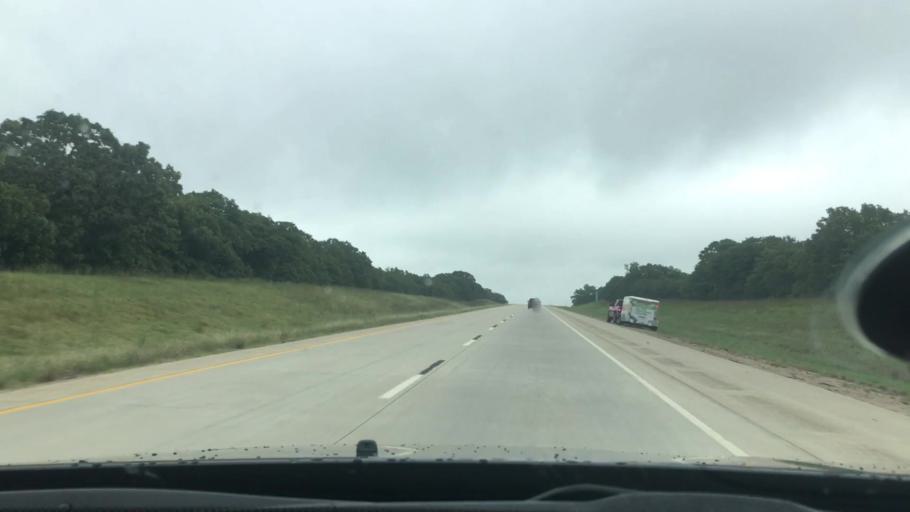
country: US
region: Oklahoma
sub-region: Okfuskee County
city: Boley
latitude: 35.3828
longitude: -96.5158
